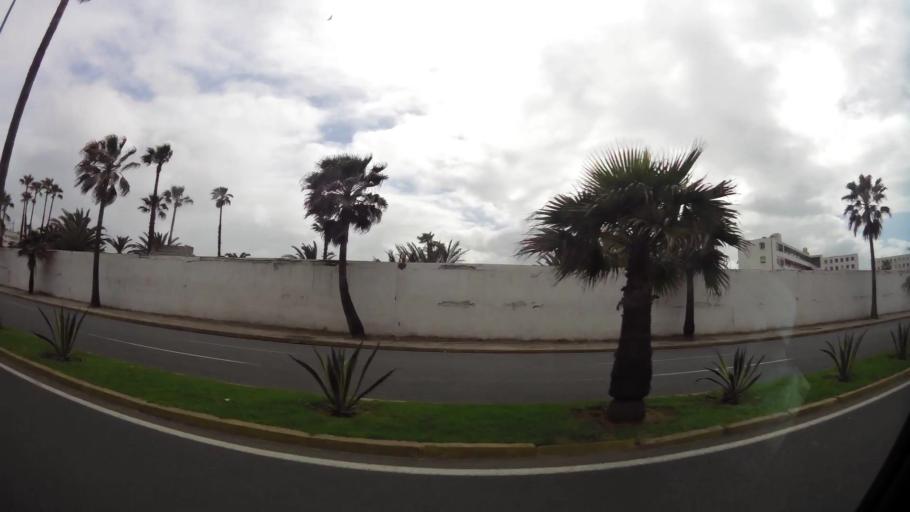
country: MA
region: Grand Casablanca
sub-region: Casablanca
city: Casablanca
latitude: 33.6057
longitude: -7.6482
